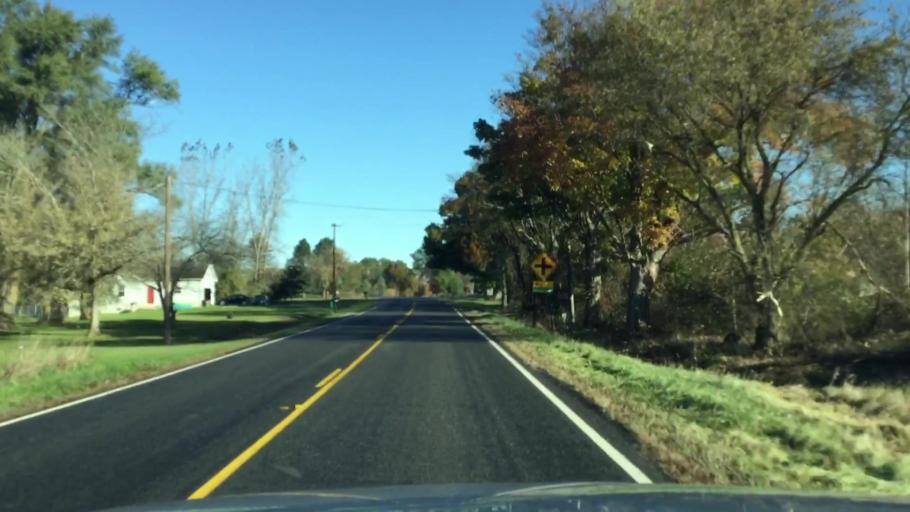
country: US
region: Michigan
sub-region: Shiawassee County
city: Durand
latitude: 42.8667
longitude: -83.9467
